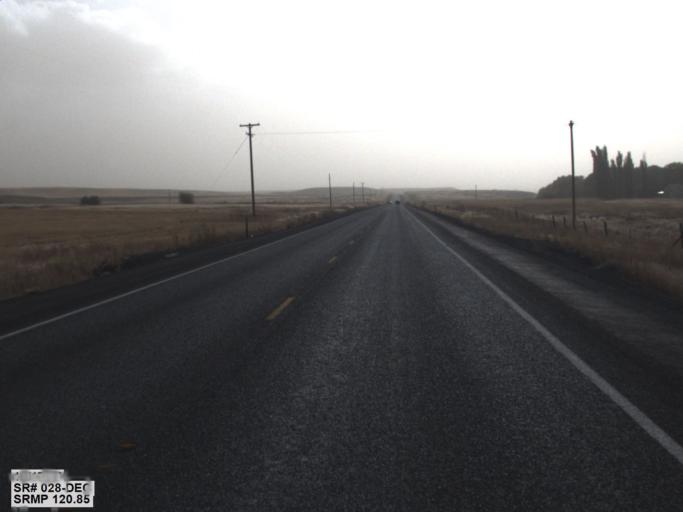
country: US
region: Washington
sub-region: Lincoln County
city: Davenport
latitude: 47.5157
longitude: -118.2170
